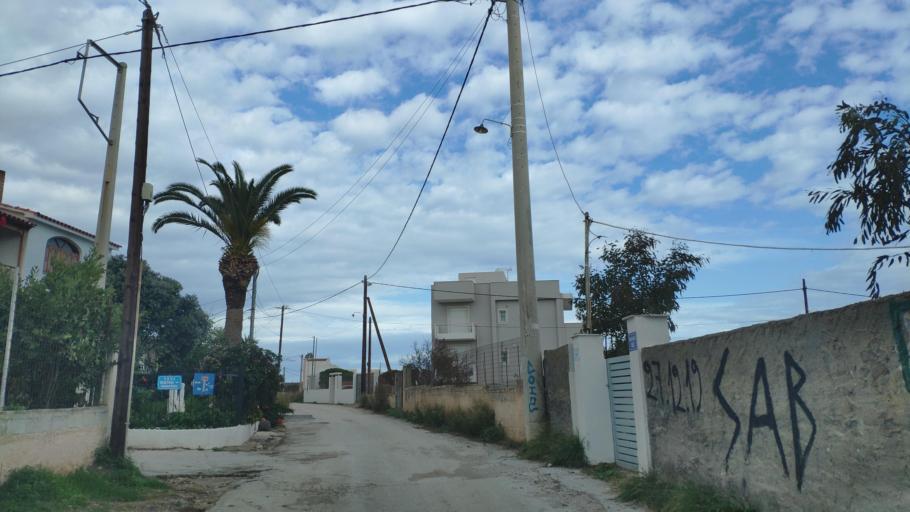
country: GR
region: Attica
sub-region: Nomarchia Anatolikis Attikis
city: Artemida
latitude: 37.9384
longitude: 24.0137
